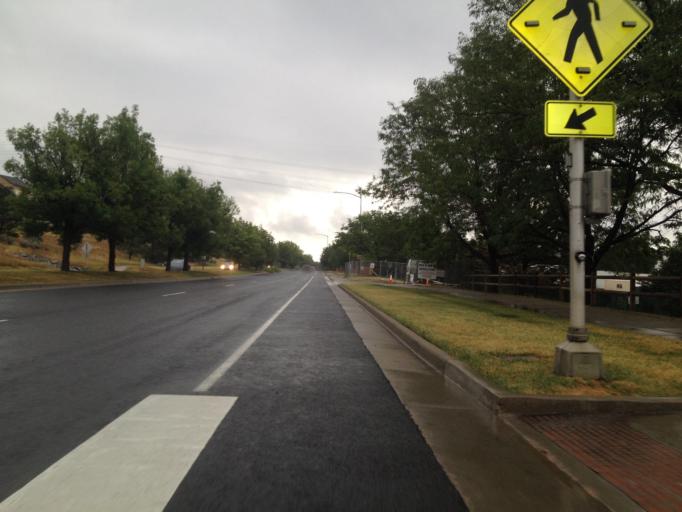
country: US
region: Colorado
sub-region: Boulder County
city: Superior
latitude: 39.9754
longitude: -105.1577
